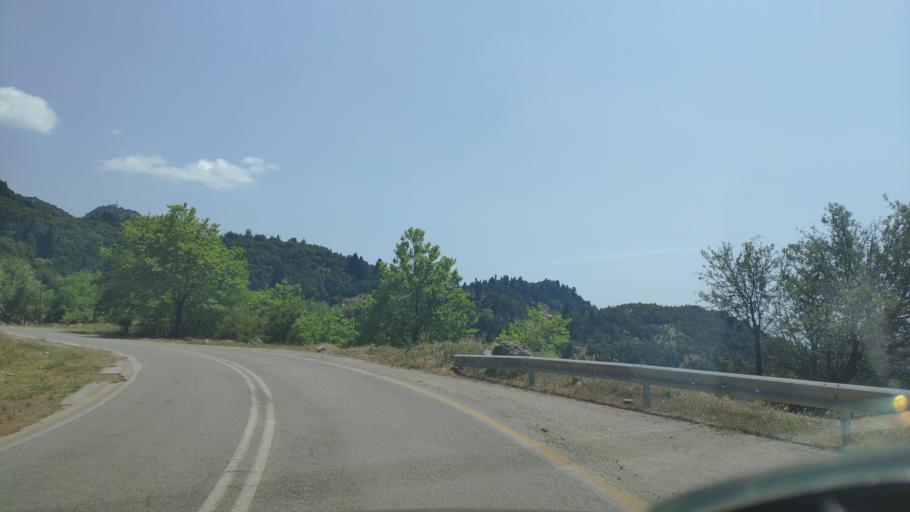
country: GR
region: Epirus
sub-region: Nomos Artas
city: Ano Kalentini
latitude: 39.2459
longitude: 21.2333
